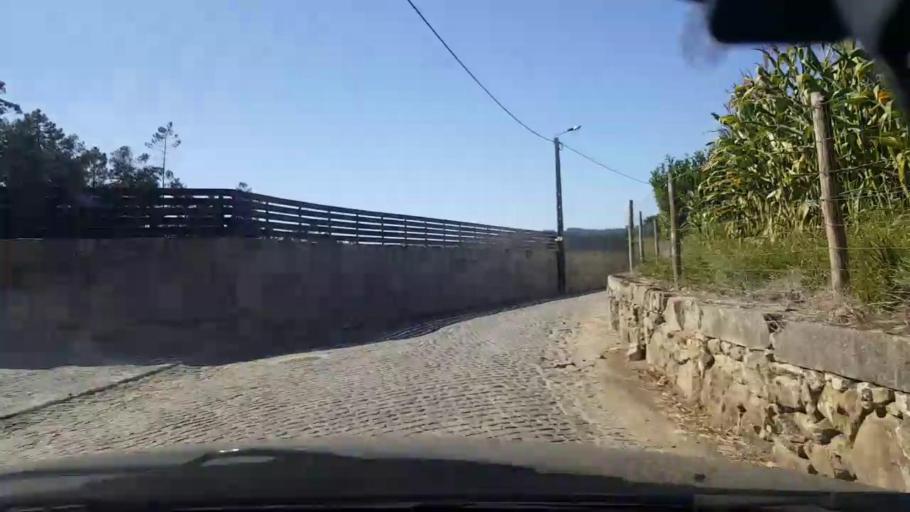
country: PT
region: Braga
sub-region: Vila Nova de Famalicao
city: Ribeirao
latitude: 41.3574
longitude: -8.6340
